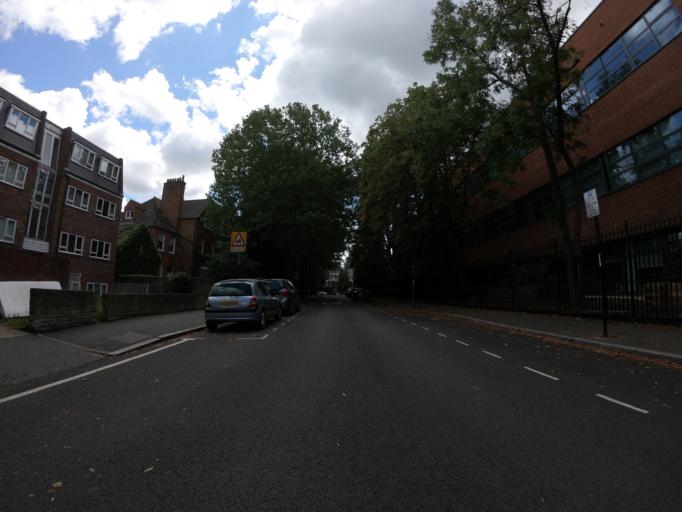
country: GB
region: England
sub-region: Greater London
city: Blackheath
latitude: 51.4780
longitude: 0.0161
